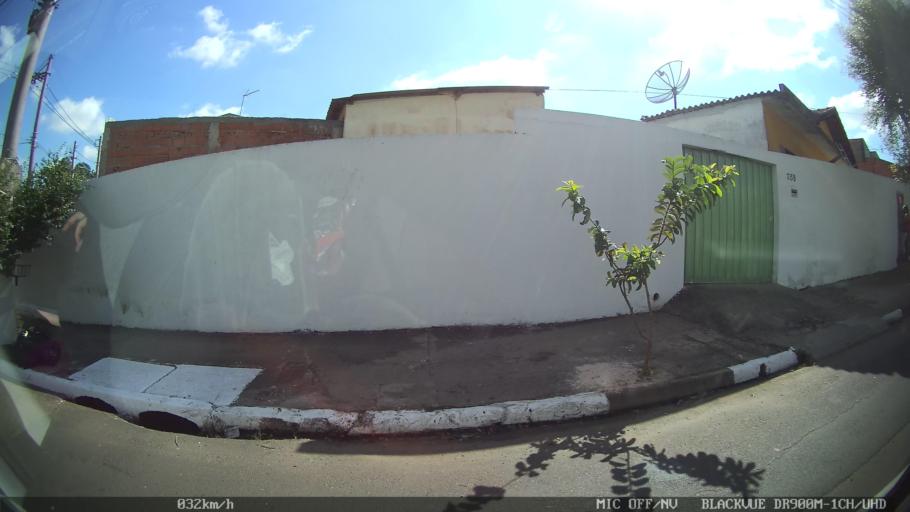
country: BR
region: Sao Paulo
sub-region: Hortolandia
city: Hortolandia
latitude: -22.8931
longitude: -47.1953
